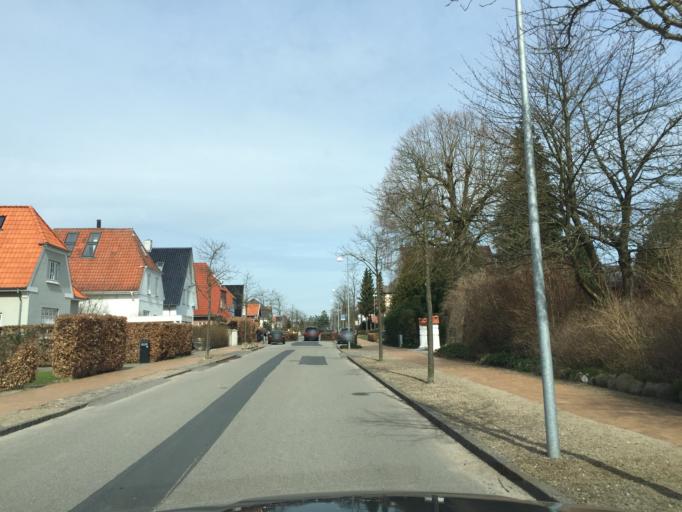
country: DK
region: South Denmark
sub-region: Odense Kommune
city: Odense
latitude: 55.3761
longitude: 10.3765
